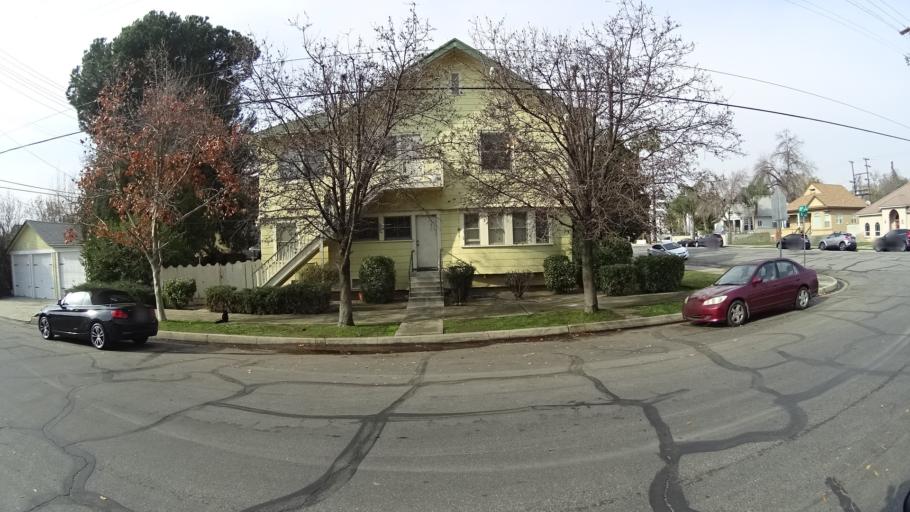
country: US
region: California
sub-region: Kern County
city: Bakersfield
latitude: 35.3760
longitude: -119.0293
